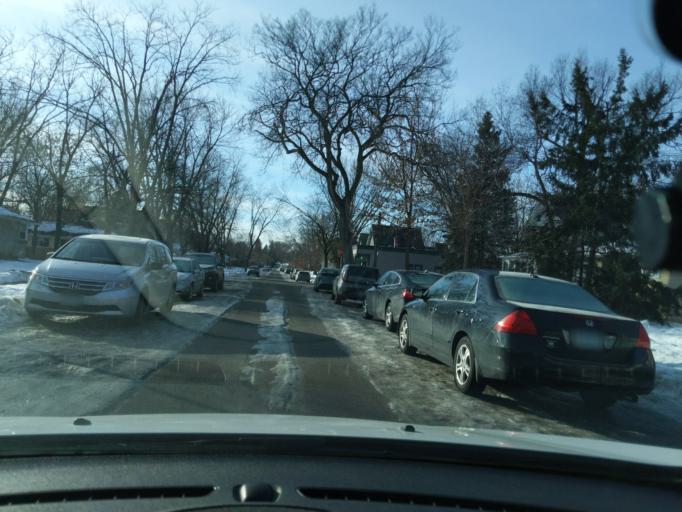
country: US
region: Minnesota
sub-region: Ramsey County
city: Lauderdale
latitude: 44.9903
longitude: -93.2177
